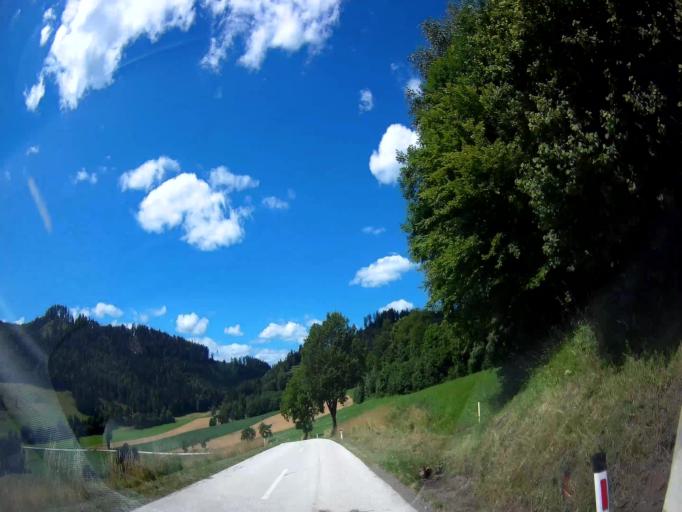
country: AT
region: Carinthia
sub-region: Politischer Bezirk Sankt Veit an der Glan
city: St. Georgen am Laengsee
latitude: 46.7199
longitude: 14.4223
